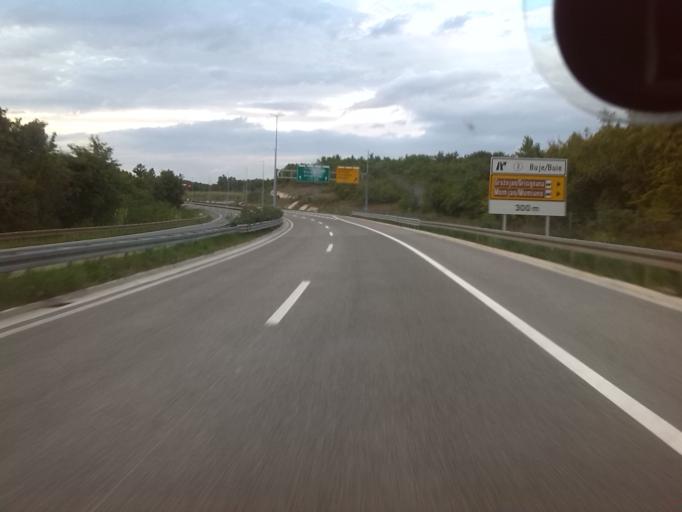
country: HR
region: Istarska
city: Buje
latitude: 45.3974
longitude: 13.6236
